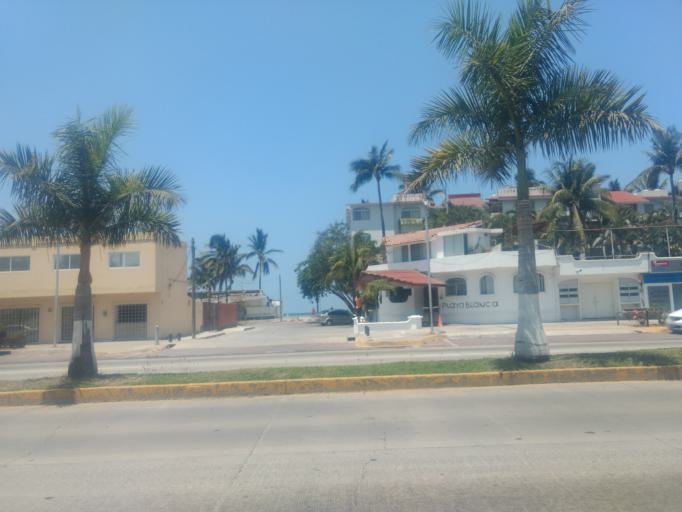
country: MX
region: Colima
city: Tapeixtles
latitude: 19.0869
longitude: -104.3104
